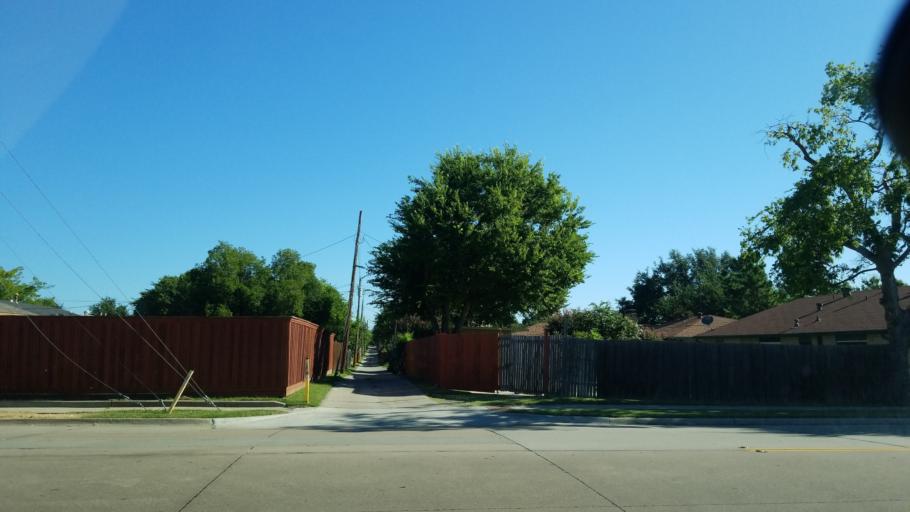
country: US
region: Texas
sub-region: Dallas County
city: Carrollton
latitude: 32.9463
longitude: -96.8875
